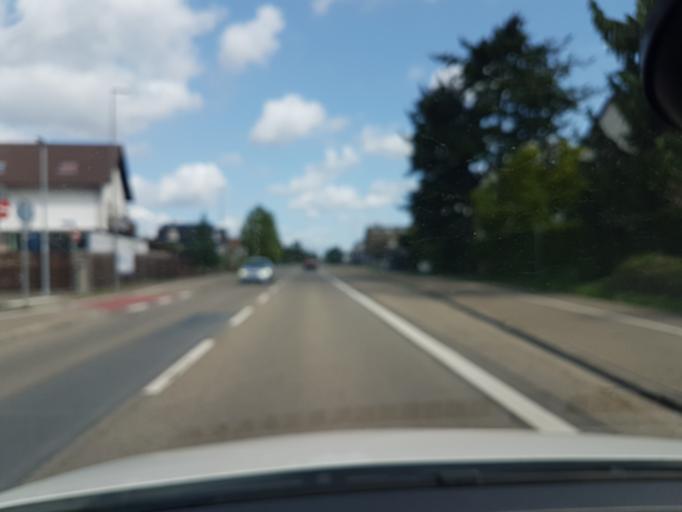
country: DE
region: Rheinland-Pfalz
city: Speyer
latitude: 49.3459
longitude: 8.4318
